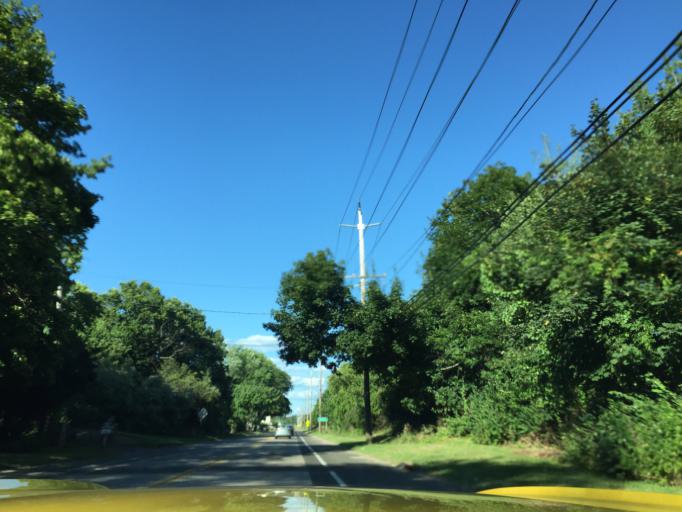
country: US
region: New York
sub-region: Suffolk County
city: Greenport West
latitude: 41.0937
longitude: -72.4020
